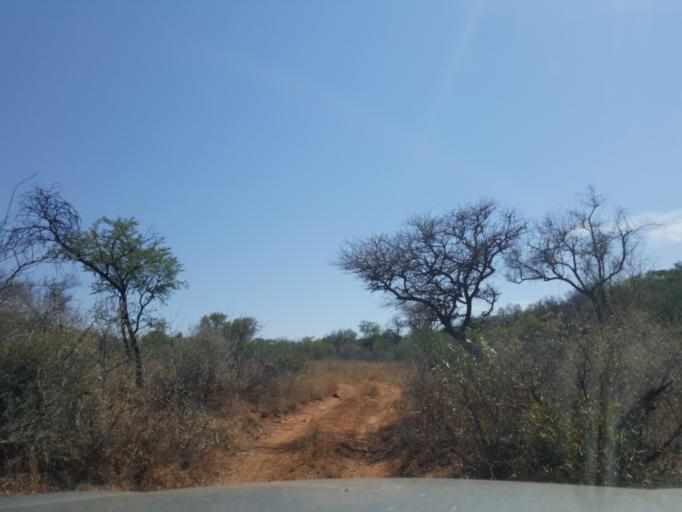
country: BW
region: South East
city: Lobatse
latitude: -25.1477
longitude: 25.6699
